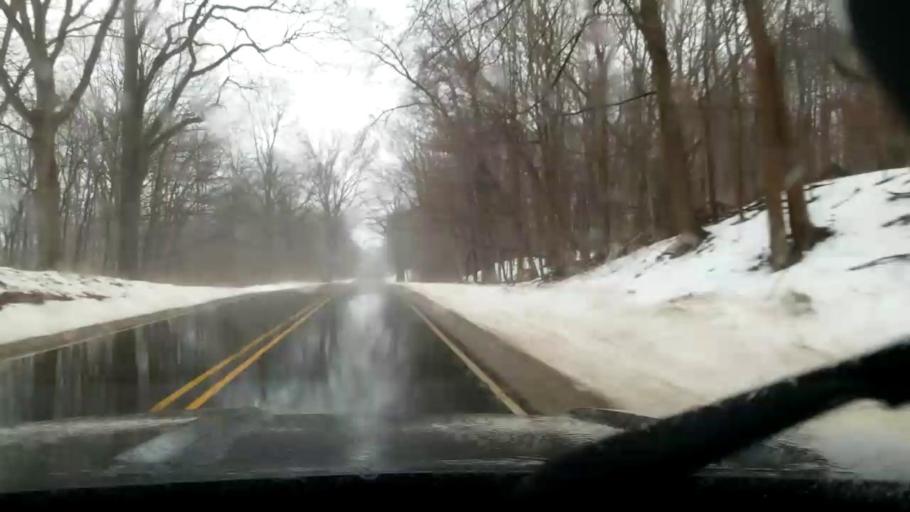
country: US
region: Michigan
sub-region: Jackson County
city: Grass Lake
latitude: 42.3243
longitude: -84.2355
